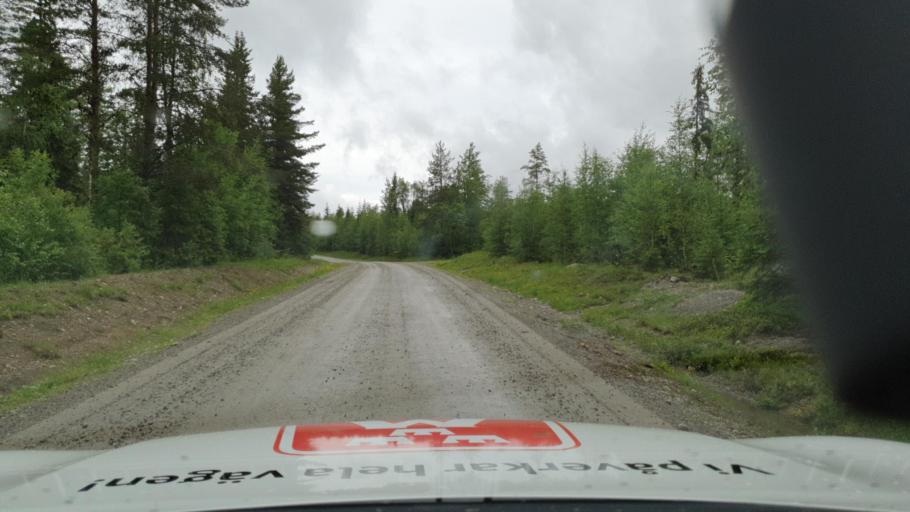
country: SE
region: Vaesterbotten
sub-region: Dorotea Kommun
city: Dorotea
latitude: 64.0577
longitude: 16.7216
